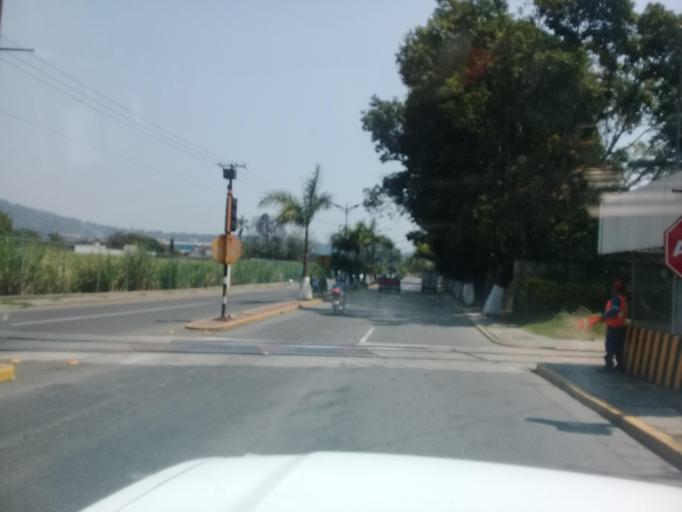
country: MX
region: Veracruz
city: Ixtac Zoquitlan
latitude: 18.8623
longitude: -97.0520
